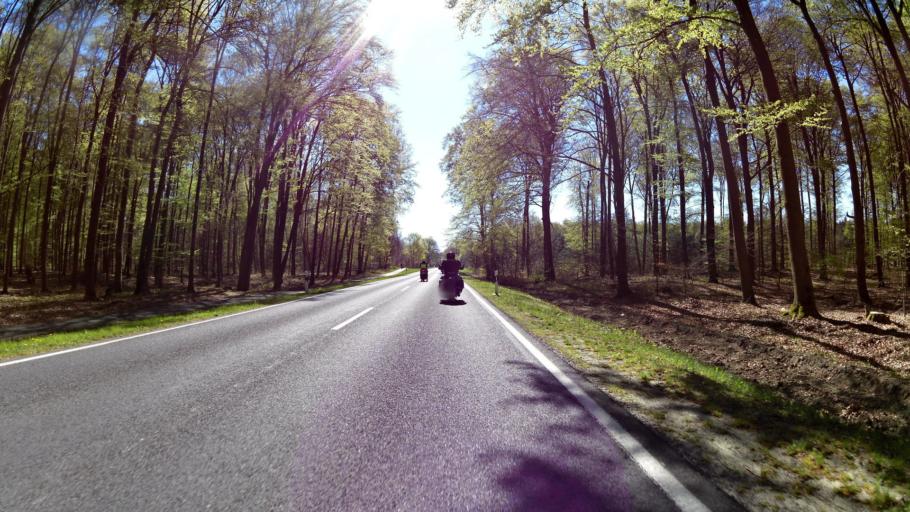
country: DE
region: Brandenburg
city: Wandlitz
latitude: 52.7192
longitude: 13.5222
